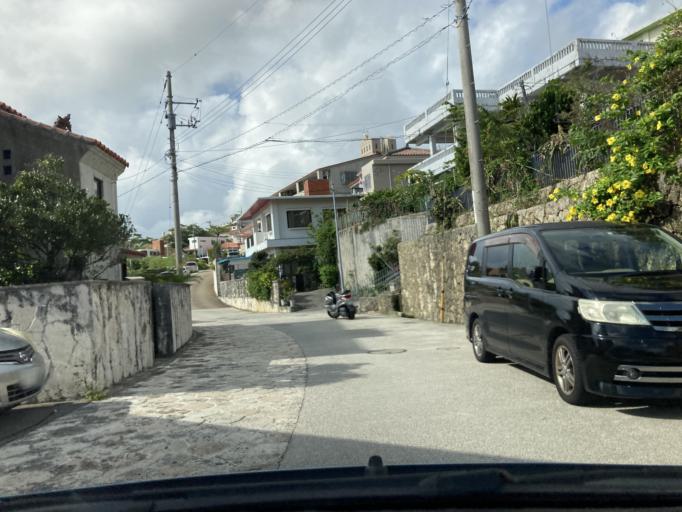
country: JP
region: Okinawa
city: Naha-shi
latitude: 26.2160
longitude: 127.7138
